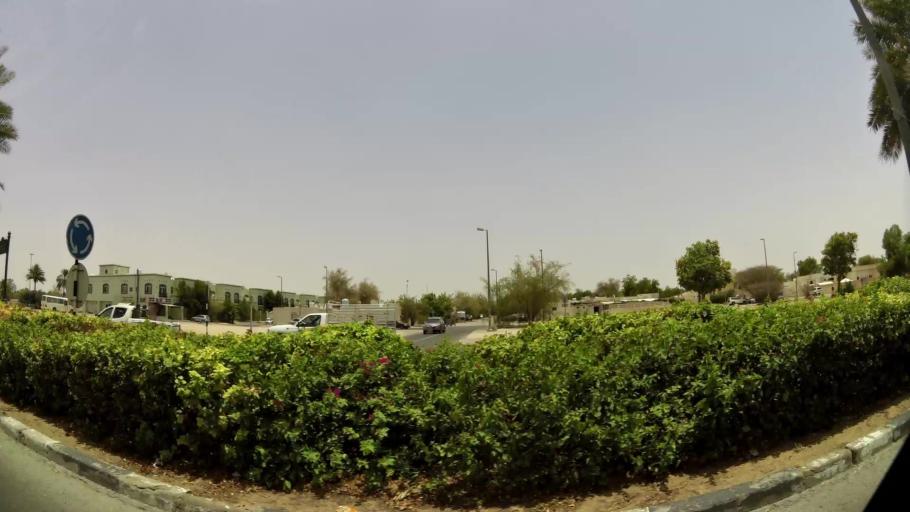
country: AE
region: Abu Dhabi
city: Al Ain
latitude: 24.2115
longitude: 55.7462
